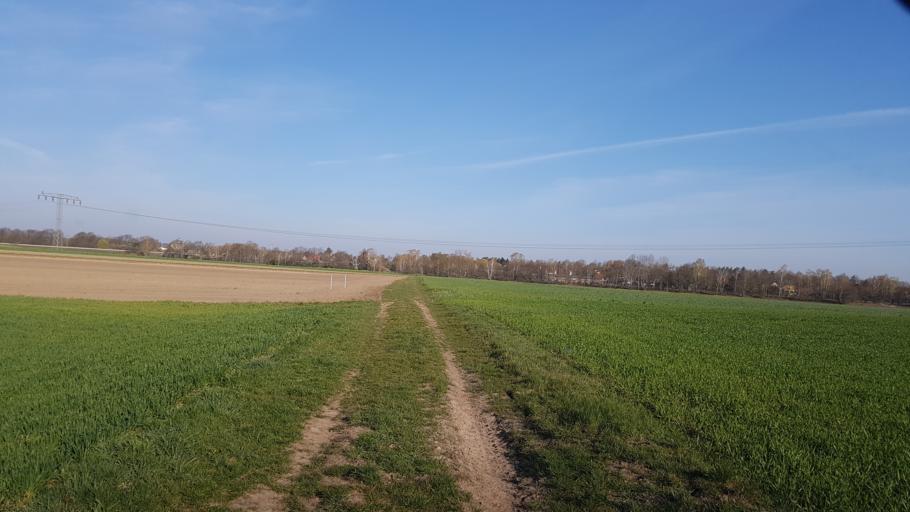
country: DE
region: Brandenburg
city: Doberlug-Kirchhain
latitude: 51.6204
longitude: 13.5820
